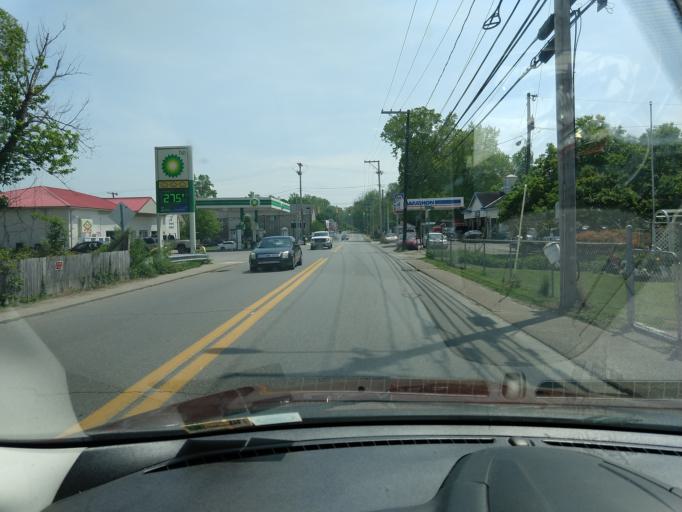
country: US
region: West Virginia
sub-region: Kanawha County
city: Saint Albans
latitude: 38.3773
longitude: -81.8081
